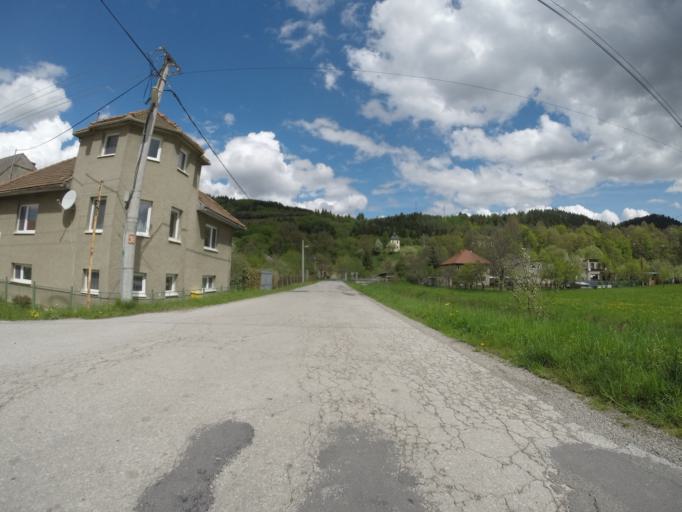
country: SK
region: Banskobystricky
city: Hrochot,Slovakia
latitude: 48.8154
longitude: 19.4320
